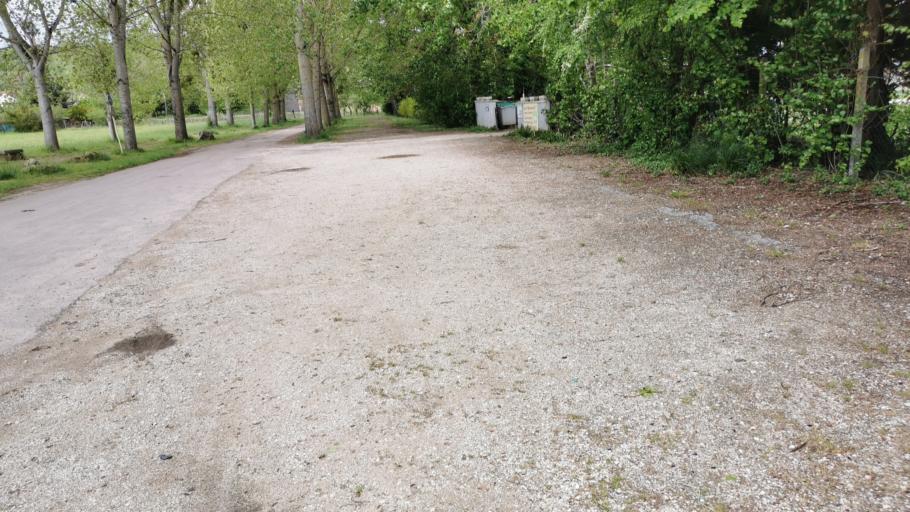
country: FR
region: Bourgogne
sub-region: Departement de l'Yonne
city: Villeneuve-sur-Yonne
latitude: 48.0808
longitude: 3.2886
